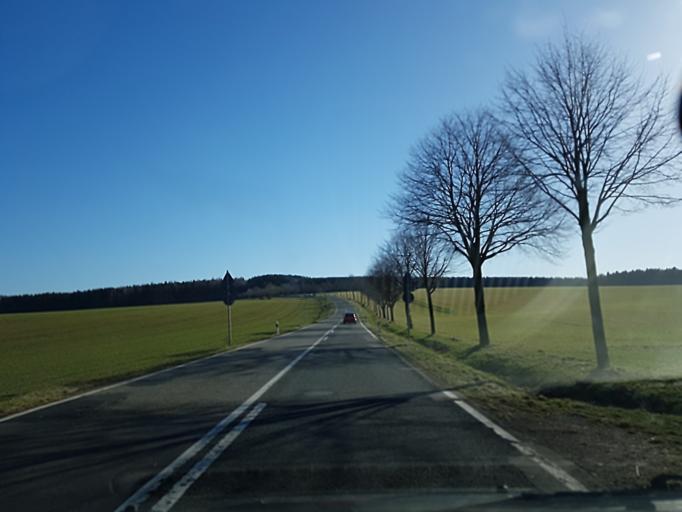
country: DE
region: Saxony
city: Oberschona
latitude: 50.8967
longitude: 13.2411
